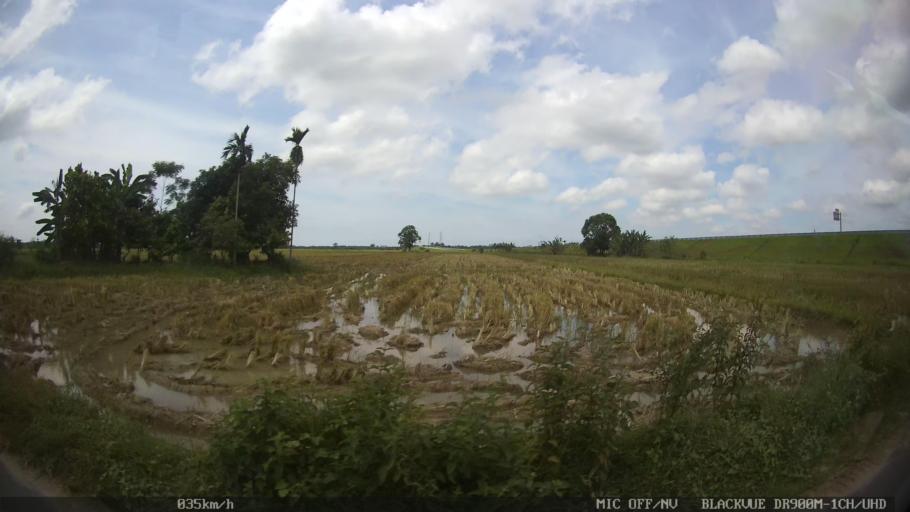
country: ID
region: North Sumatra
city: Percut
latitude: 3.5721
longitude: 98.8460
